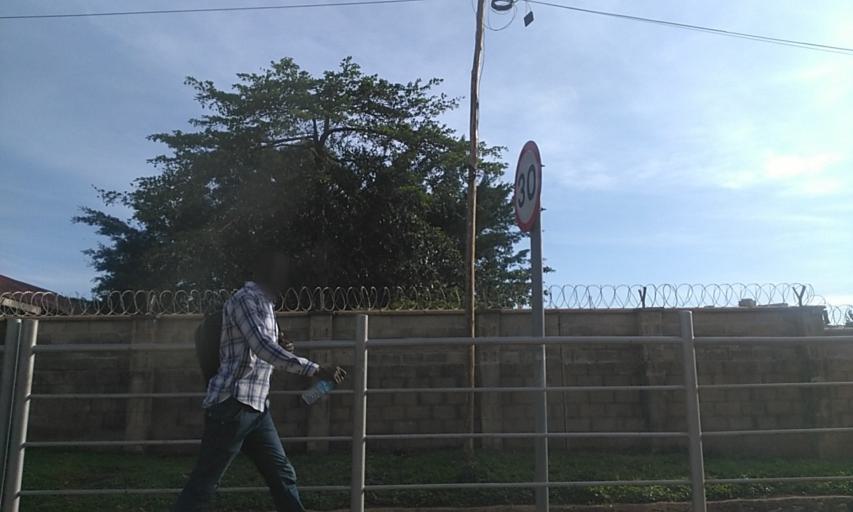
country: UG
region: Central Region
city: Kampala Central Division
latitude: 0.3217
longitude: 32.5714
